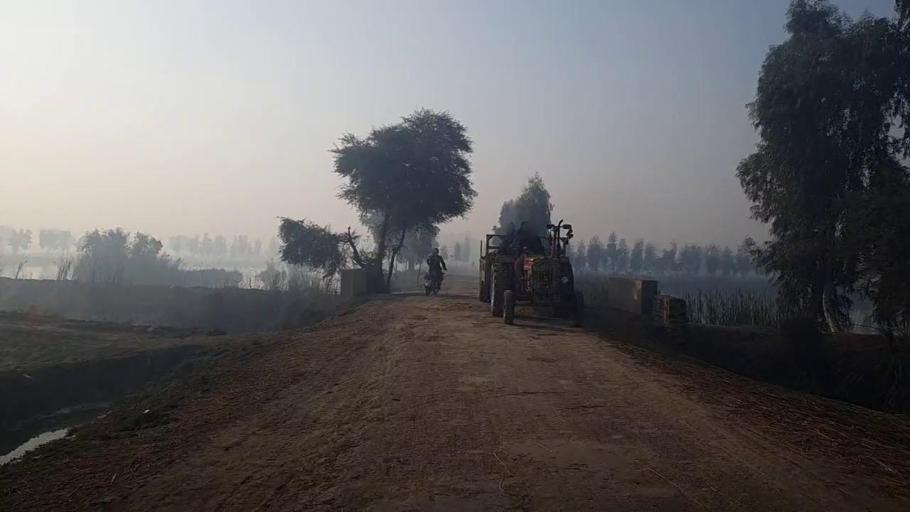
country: PK
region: Sindh
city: Mehar
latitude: 27.1534
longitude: 67.8239
